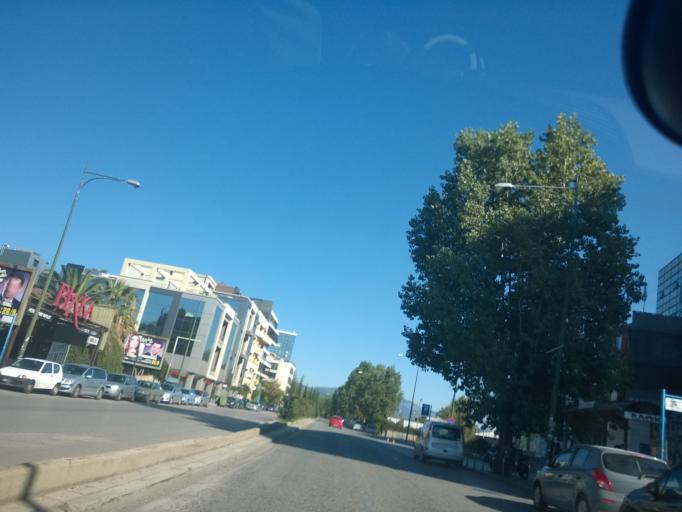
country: GR
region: Central Macedonia
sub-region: Nomos Thessalonikis
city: Thessaloniki
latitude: 40.6408
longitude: 22.9188
